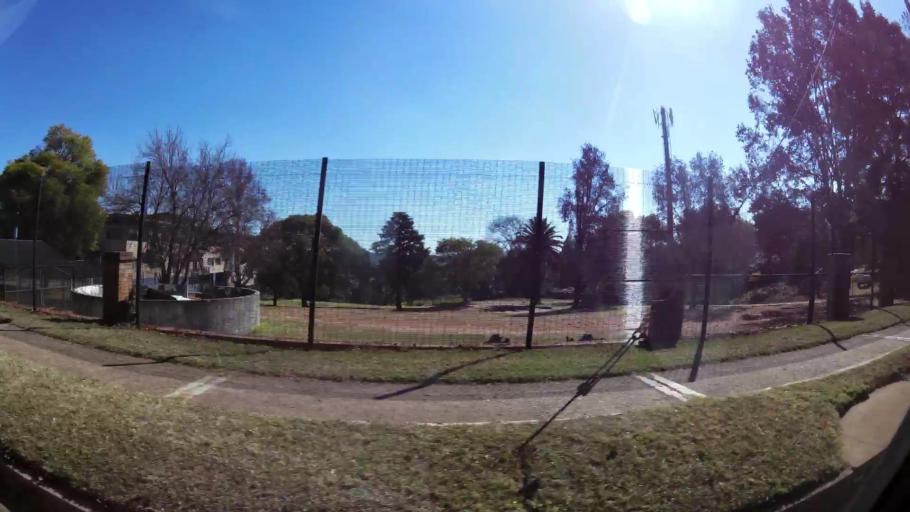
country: ZA
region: Gauteng
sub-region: City of Johannesburg Metropolitan Municipality
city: Roodepoort
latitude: -26.1659
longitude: 27.9312
